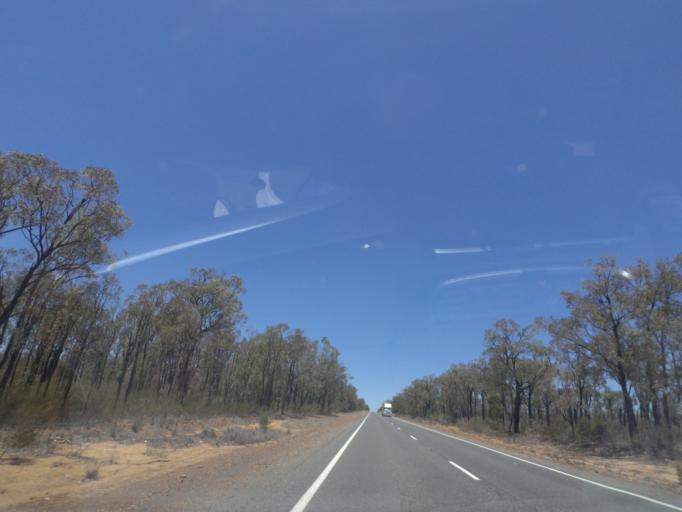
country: AU
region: New South Wales
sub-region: Narrabri
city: Narrabri
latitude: -30.6983
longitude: 149.5357
